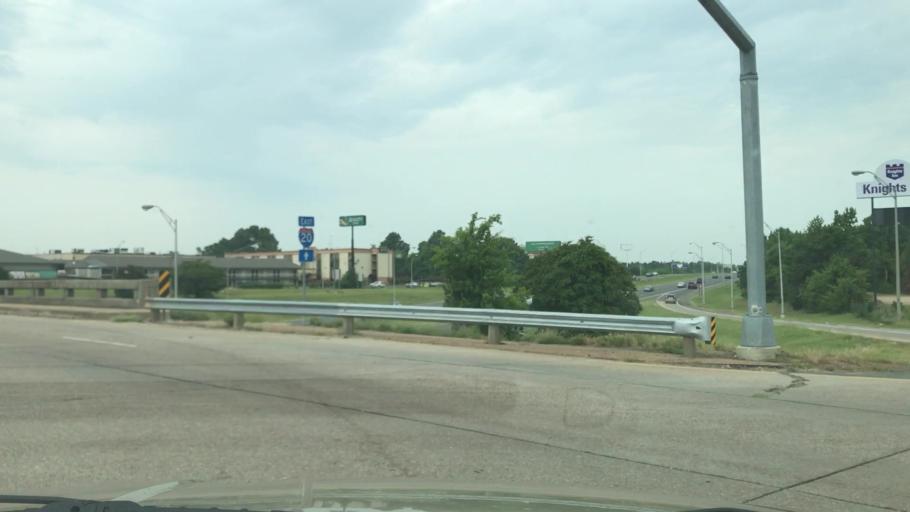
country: US
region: Louisiana
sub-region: Caddo Parish
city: Shreveport
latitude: 32.4623
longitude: -93.8275
